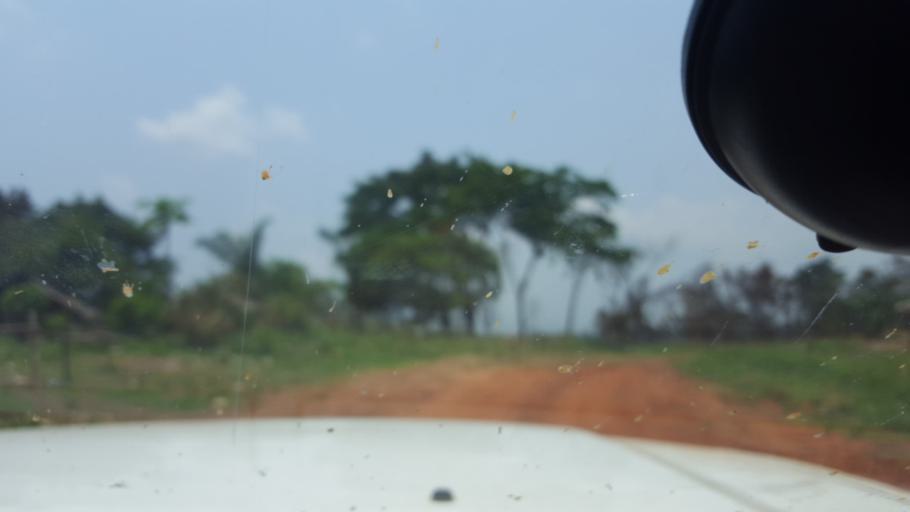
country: CD
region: Bandundu
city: Mushie
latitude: -3.7507
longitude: 16.6285
